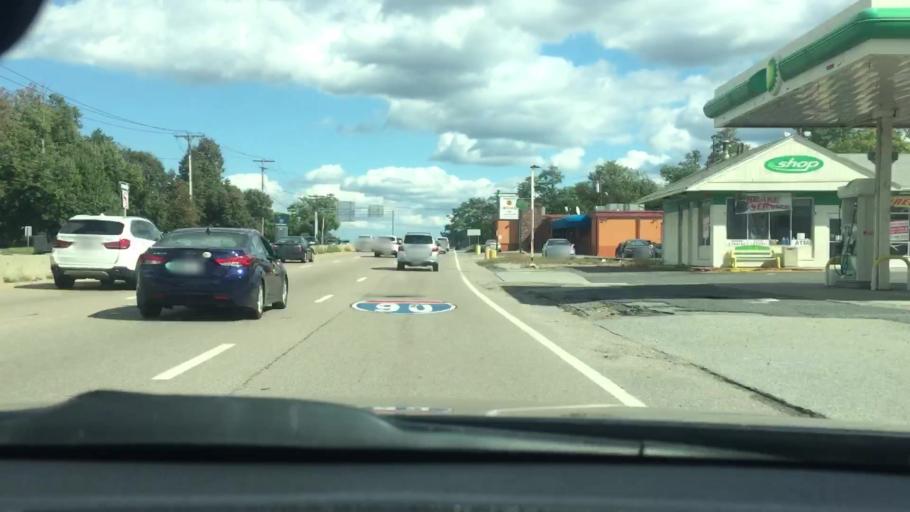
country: US
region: Massachusetts
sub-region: Worcester County
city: Southborough
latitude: 42.2953
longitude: -71.4925
